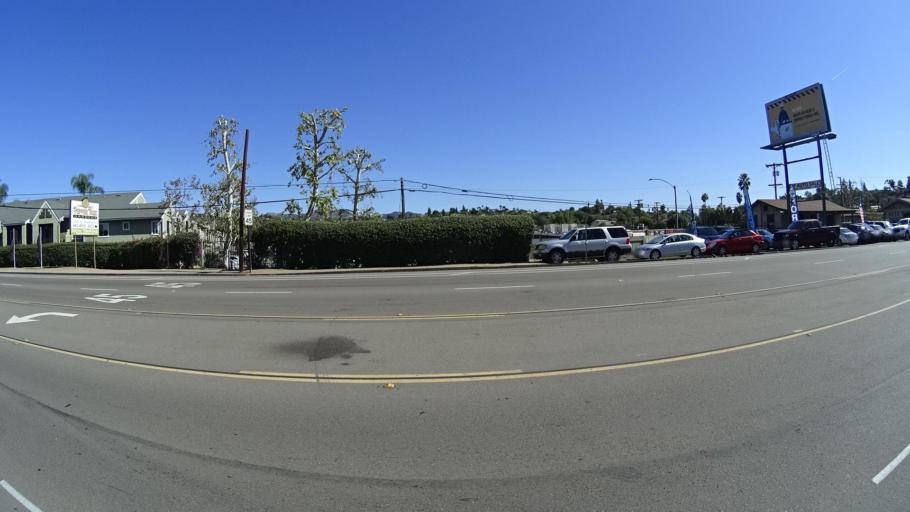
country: US
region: California
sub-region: San Diego County
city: Winter Gardens
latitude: 32.8218
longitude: -116.9339
